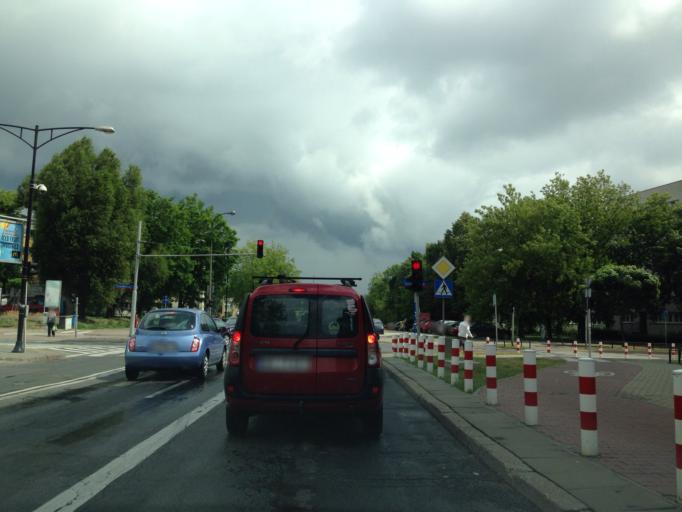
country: PL
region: Masovian Voivodeship
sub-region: Warszawa
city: Bielany
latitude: 52.2678
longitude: 20.9474
